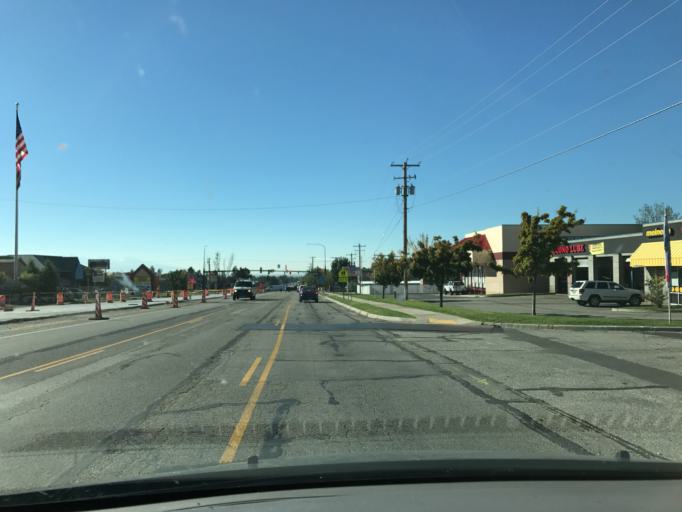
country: US
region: Utah
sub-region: Davis County
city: Hill Air Force Bace
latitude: 41.0909
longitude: -111.9736
